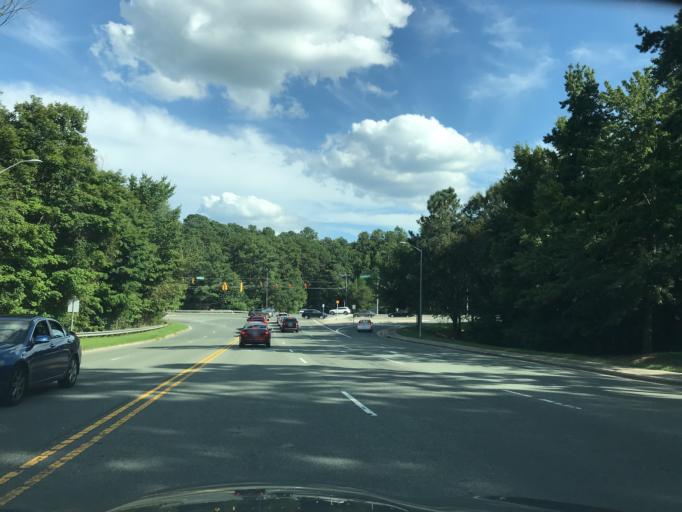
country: US
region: North Carolina
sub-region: Orange County
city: Chapel Hill
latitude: 35.8992
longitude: -79.0371
